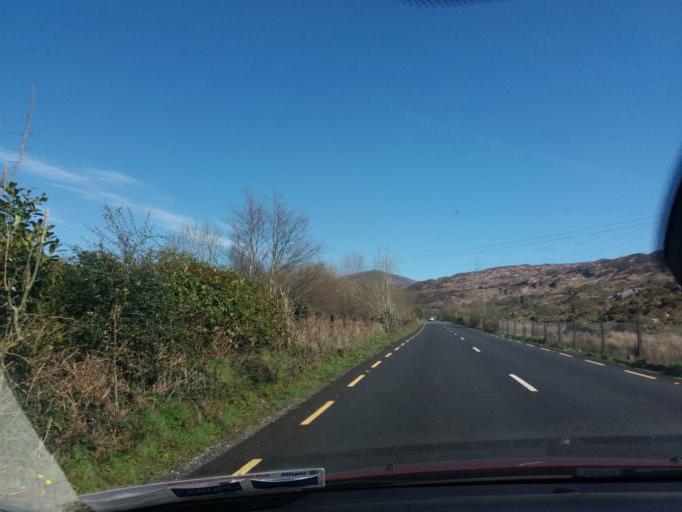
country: IE
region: Munster
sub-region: Ciarrai
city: Cill Airne
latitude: 51.9314
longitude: -9.3831
